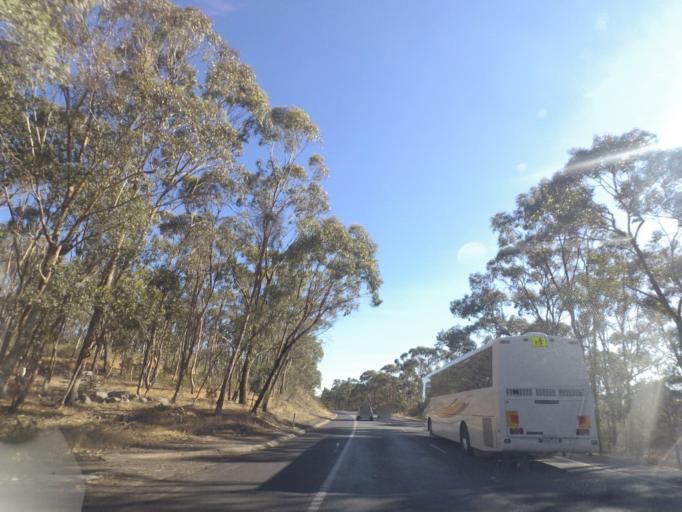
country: AU
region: Victoria
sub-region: Murrindindi
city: Kinglake West
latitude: -37.1781
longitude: 145.0706
